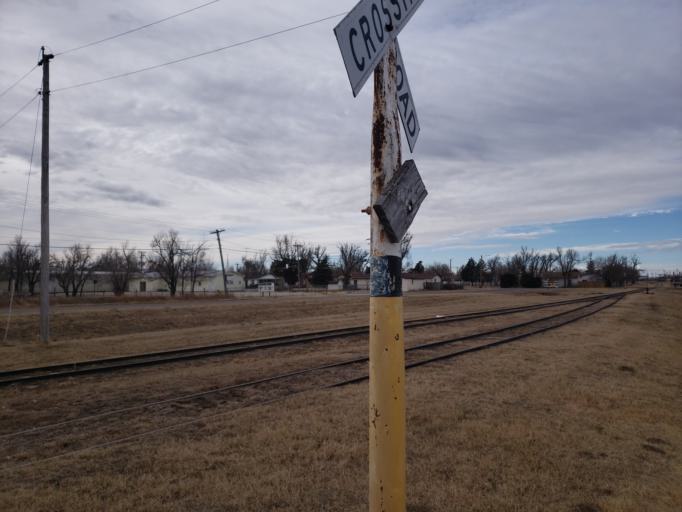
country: US
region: Kansas
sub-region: Ford County
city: Dodge City
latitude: 37.7420
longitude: -100.0132
